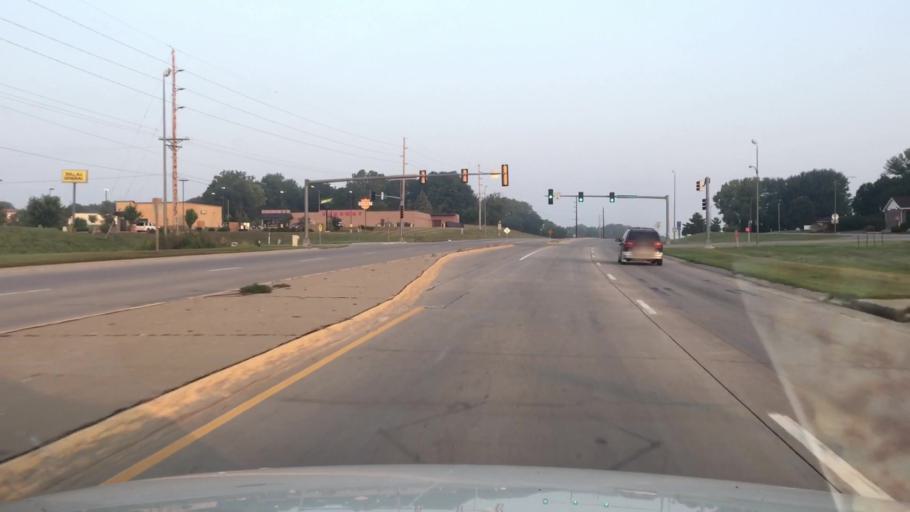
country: US
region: Iowa
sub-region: Warren County
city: Carlisle
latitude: 41.4983
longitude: -93.4969
